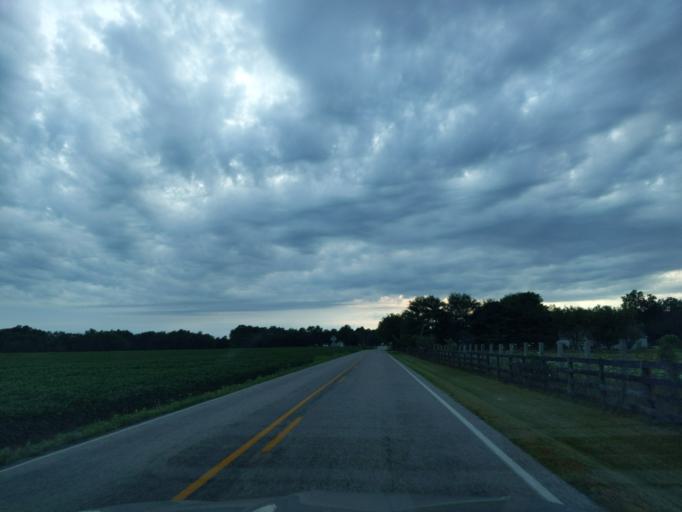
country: US
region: Indiana
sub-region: Ripley County
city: Sunman
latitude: 39.2022
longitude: -85.1752
